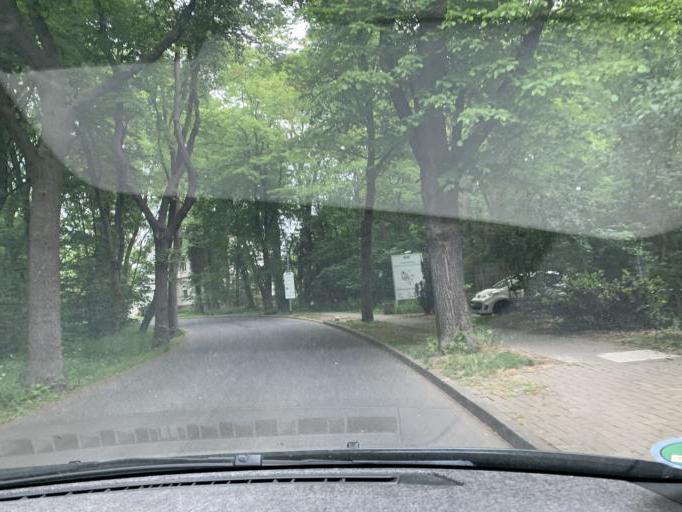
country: DE
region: North Rhine-Westphalia
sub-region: Regierungsbezirk Koln
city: Dueren
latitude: 50.8146
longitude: 6.4817
